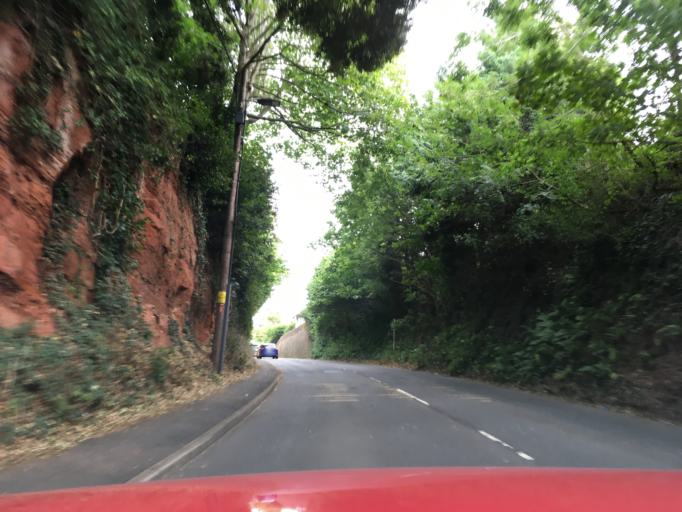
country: GB
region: England
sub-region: Devon
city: Starcross
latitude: 50.6394
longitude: -3.4710
